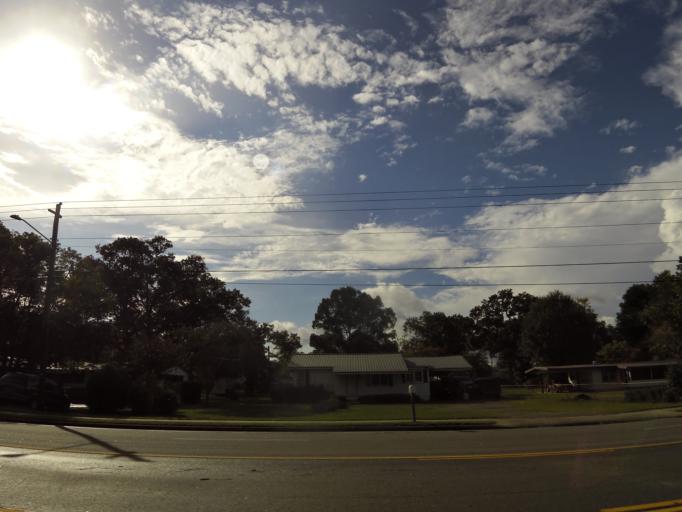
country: US
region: Georgia
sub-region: Liberty County
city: Walthourville
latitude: 31.7999
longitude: -81.6057
